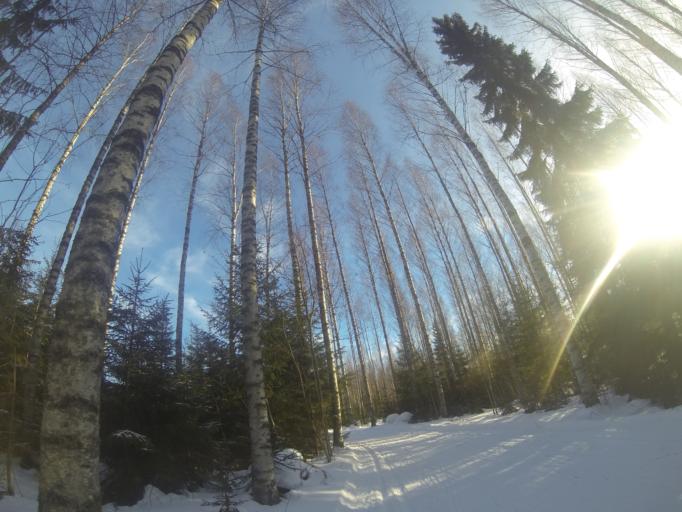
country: FI
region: Southern Savonia
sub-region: Savonlinna
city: Savonlinna
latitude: 61.8998
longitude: 28.9166
